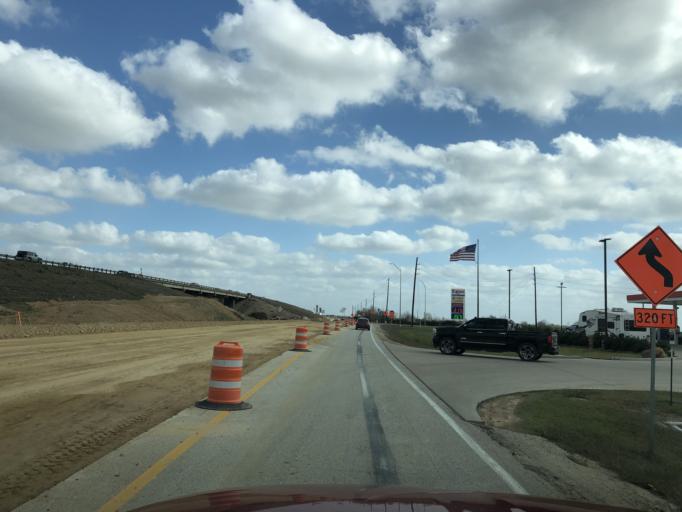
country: US
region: Texas
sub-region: Austin County
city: Sealy
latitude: 29.7630
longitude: -96.1873
